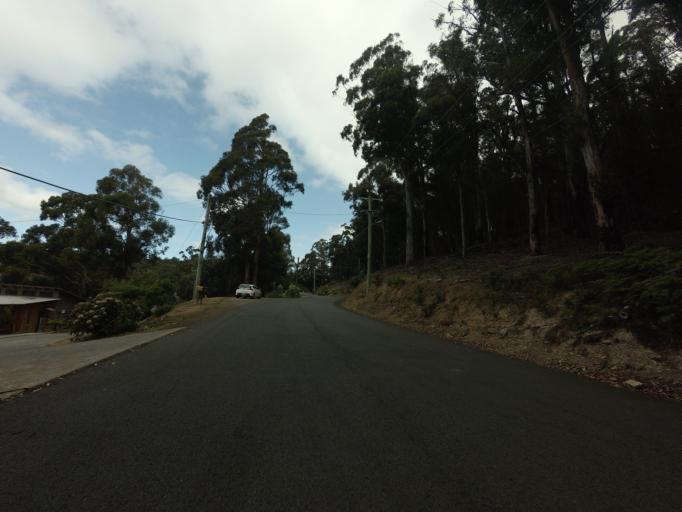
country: AU
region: Tasmania
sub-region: Hobart
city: Dynnyrne
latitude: -42.9099
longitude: 147.2674
